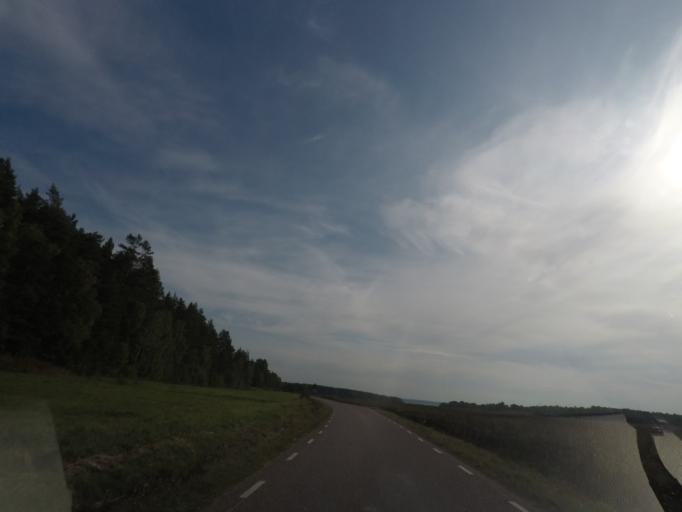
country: SE
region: Vaestmanland
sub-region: Kungsors Kommun
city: Kungsoer
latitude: 59.4960
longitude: 16.1529
